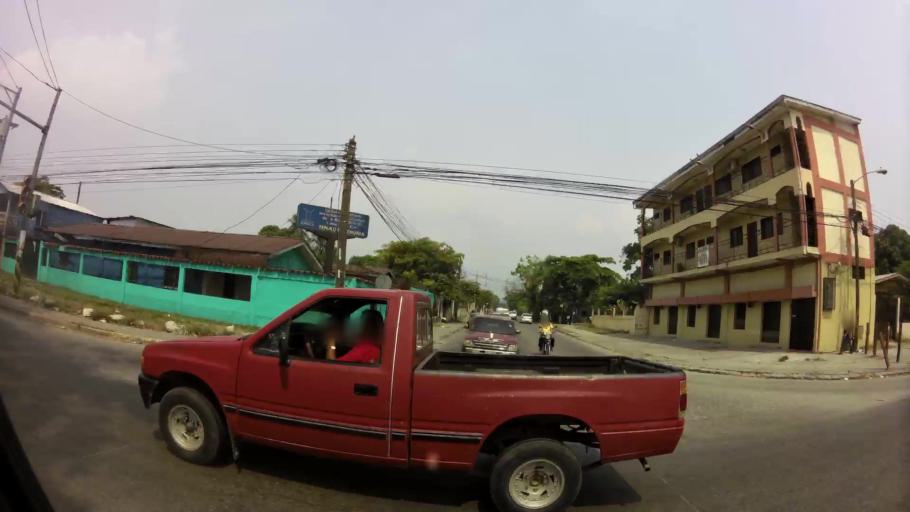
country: HN
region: Cortes
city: San Pedro Sula
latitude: 15.4889
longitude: -88.0063
